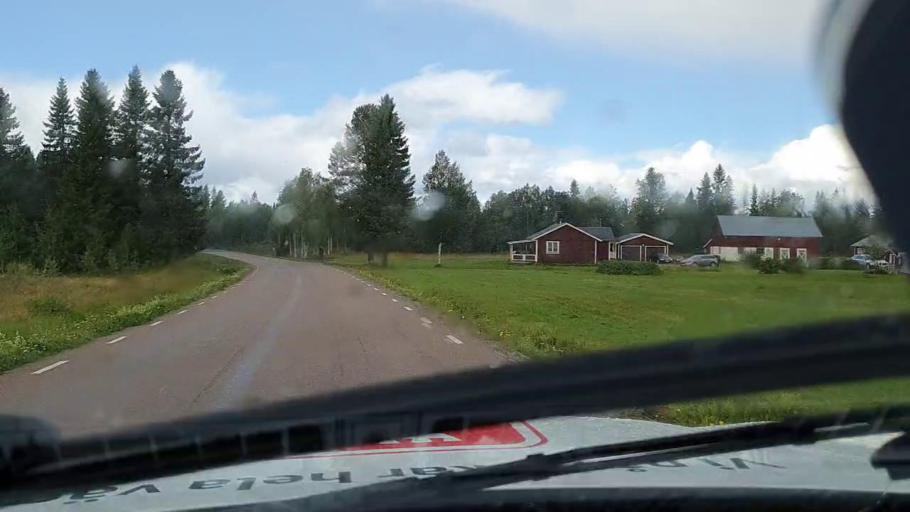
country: SE
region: Jaemtland
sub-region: Stroemsunds Kommun
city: Stroemsund
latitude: 63.8774
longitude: 15.3571
